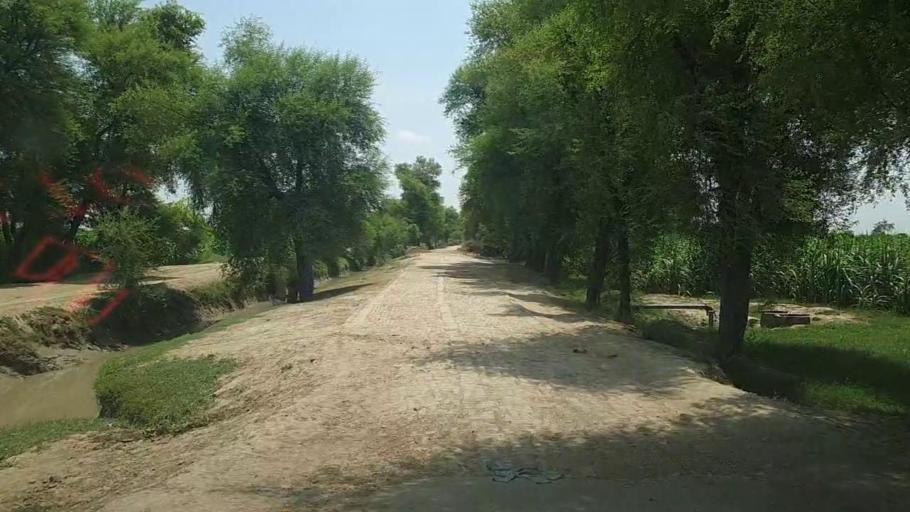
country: PK
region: Sindh
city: Ubauro
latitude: 28.2776
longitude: 69.8100
